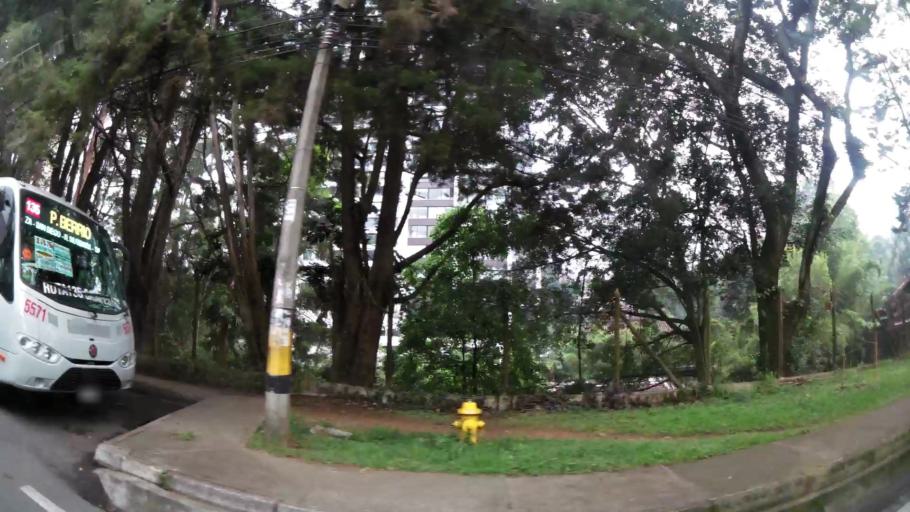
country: CO
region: Antioquia
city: Envigado
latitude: 6.1813
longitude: -75.5657
